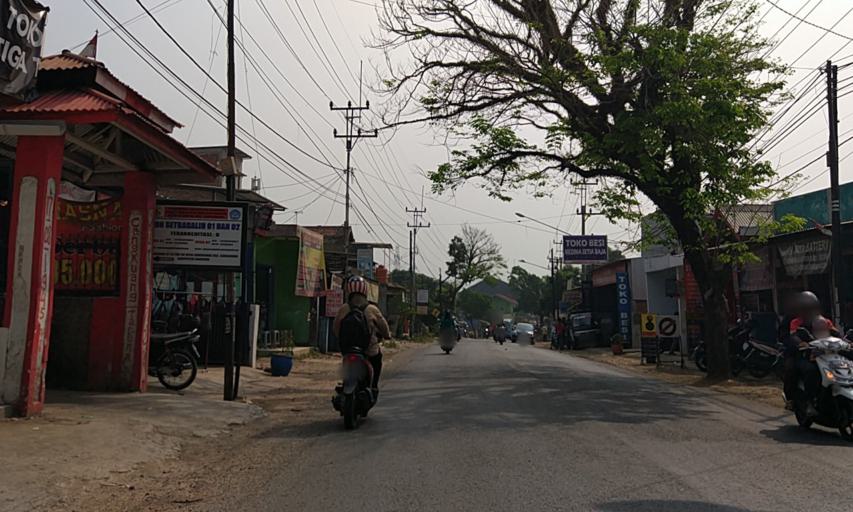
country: ID
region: West Java
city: Banjaran
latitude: -7.0439
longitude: 107.5574
